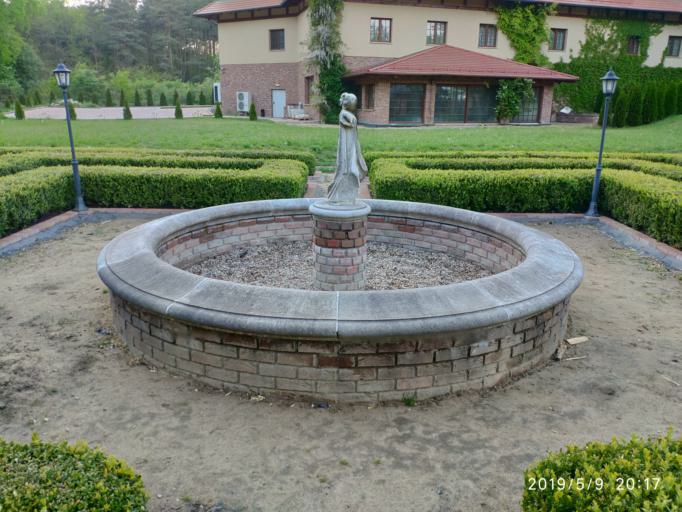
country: PL
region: Lubusz
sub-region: Zielona Gora
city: Zielona Gora
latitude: 51.9220
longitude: 15.5464
